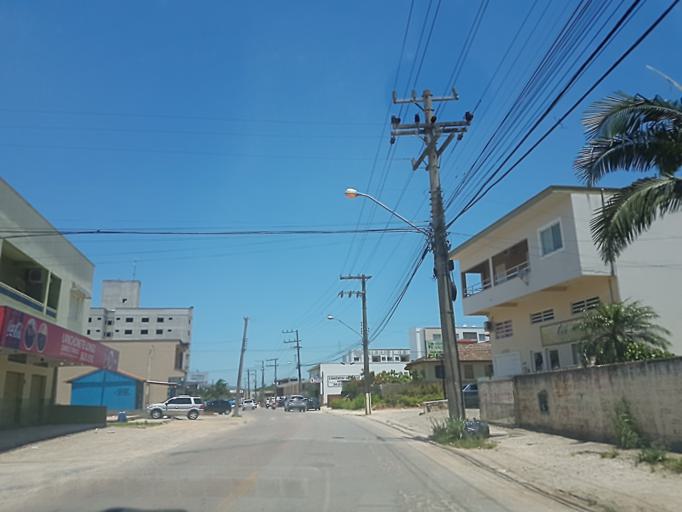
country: BR
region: Santa Catarina
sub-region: Tubarao
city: Tubarao
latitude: -28.4721
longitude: -49.0334
